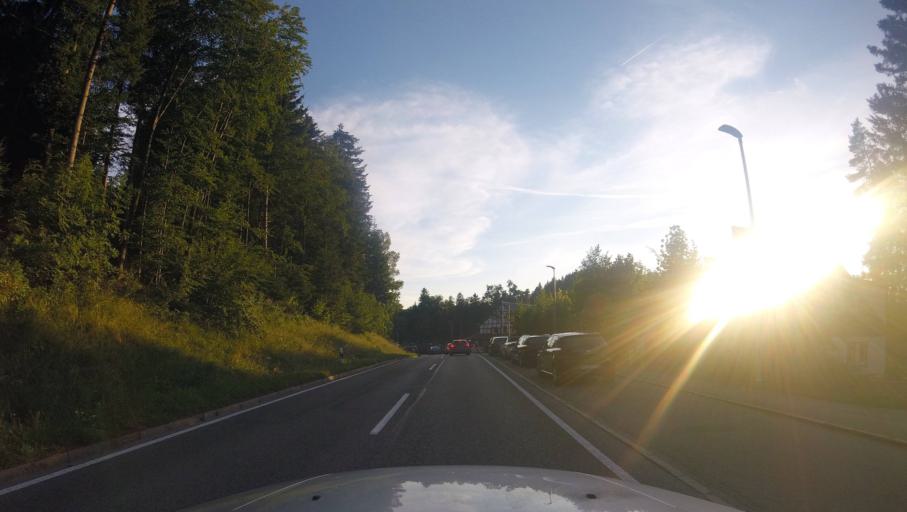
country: DE
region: Baden-Wuerttemberg
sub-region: Regierungsbezirk Stuttgart
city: Kaisersbach
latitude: 48.9205
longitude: 9.6125
